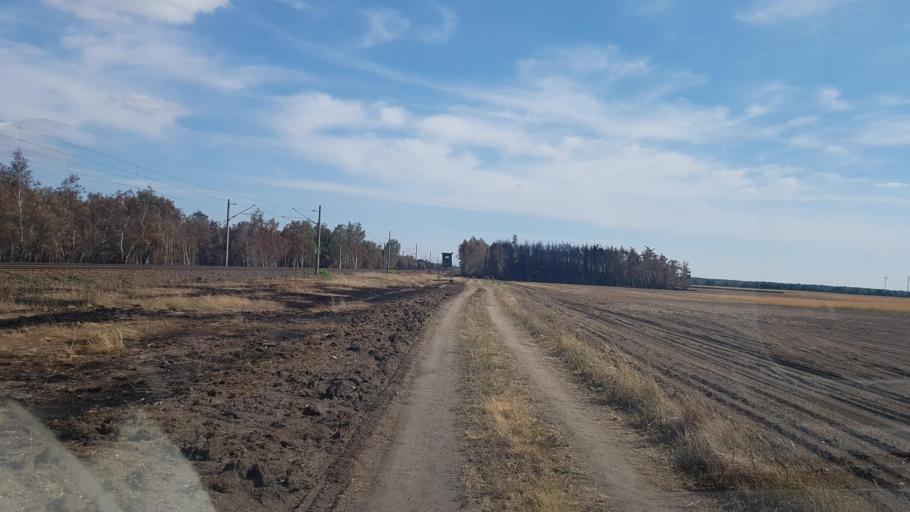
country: DE
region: Brandenburg
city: Muhlberg
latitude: 51.4322
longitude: 13.3043
